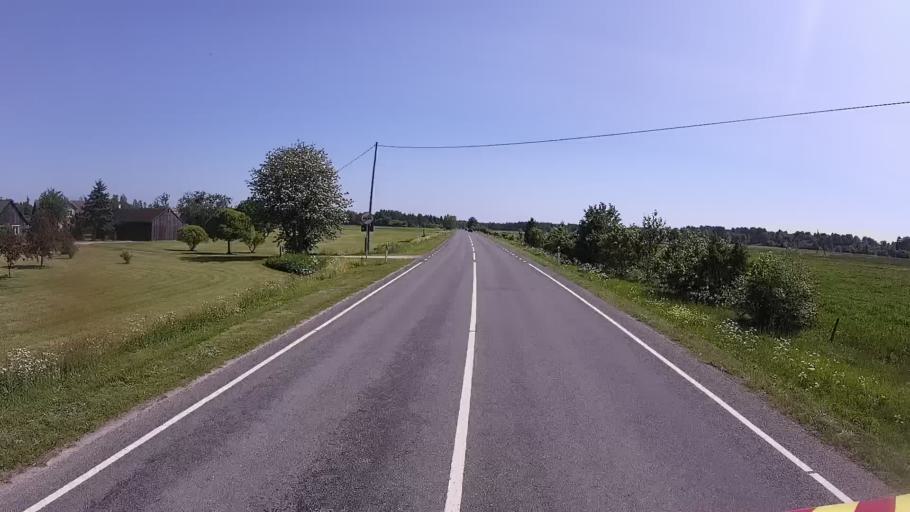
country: EE
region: Saare
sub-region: Kuressaare linn
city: Kuressaare
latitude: 58.3335
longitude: 22.4537
